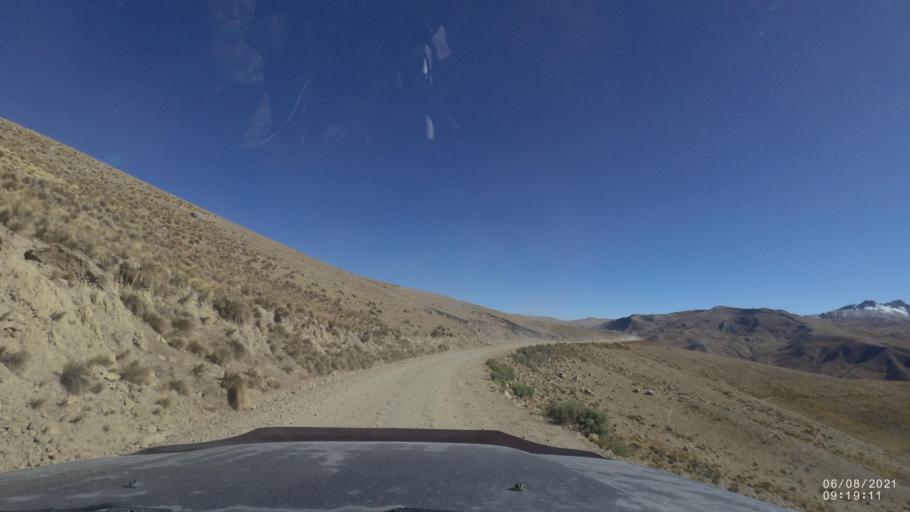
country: BO
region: Cochabamba
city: Colchani
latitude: -17.0314
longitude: -66.5320
